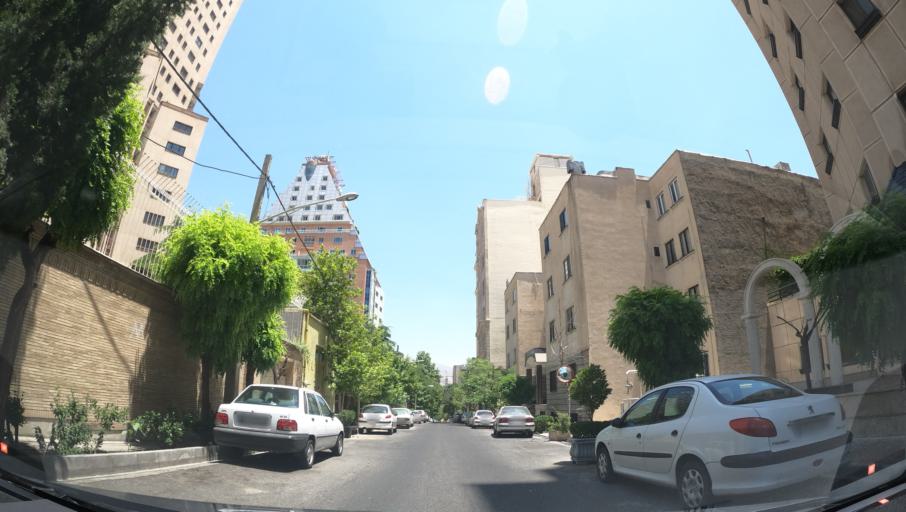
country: IR
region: Tehran
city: Tajrish
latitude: 35.8079
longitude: 51.3989
